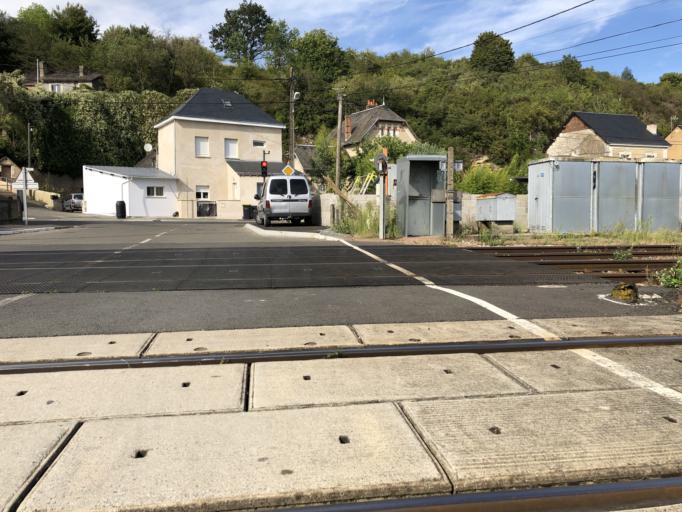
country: FR
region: Pays de la Loire
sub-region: Departement de la Sarthe
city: Chateau-du-Loir
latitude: 47.6824
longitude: 0.4260
